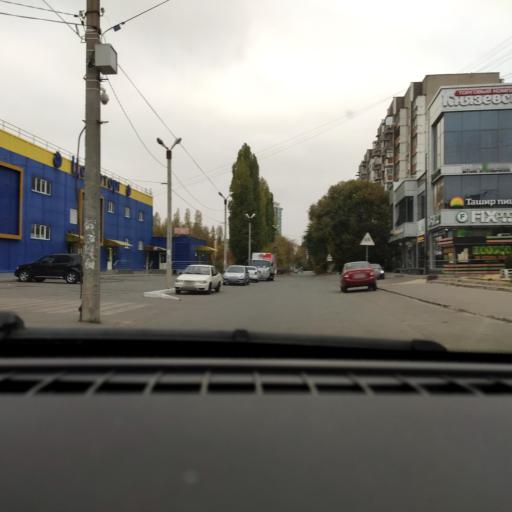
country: RU
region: Voronezj
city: Podgornoye
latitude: 51.7140
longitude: 39.1675
